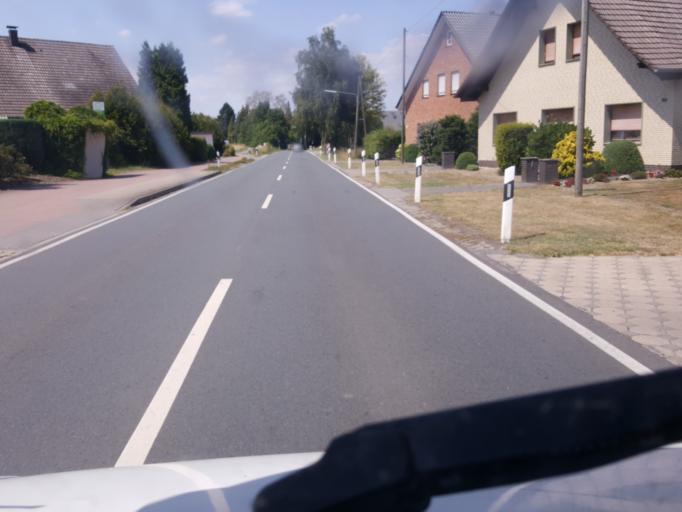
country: DE
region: North Rhine-Westphalia
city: Bad Oeynhausen
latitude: 52.2326
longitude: 8.7565
